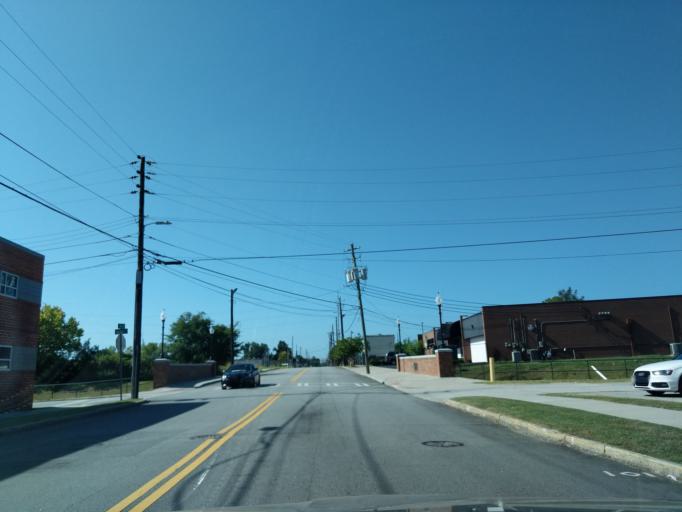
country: US
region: Georgia
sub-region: Richmond County
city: Augusta
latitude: 33.4734
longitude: -81.9729
